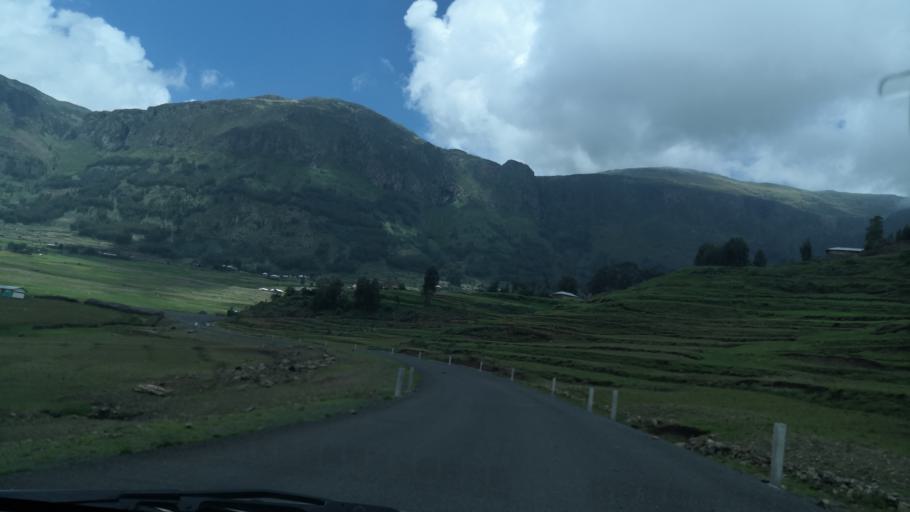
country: ET
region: Amhara
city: Kemise
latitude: 10.3606
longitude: 39.8278
